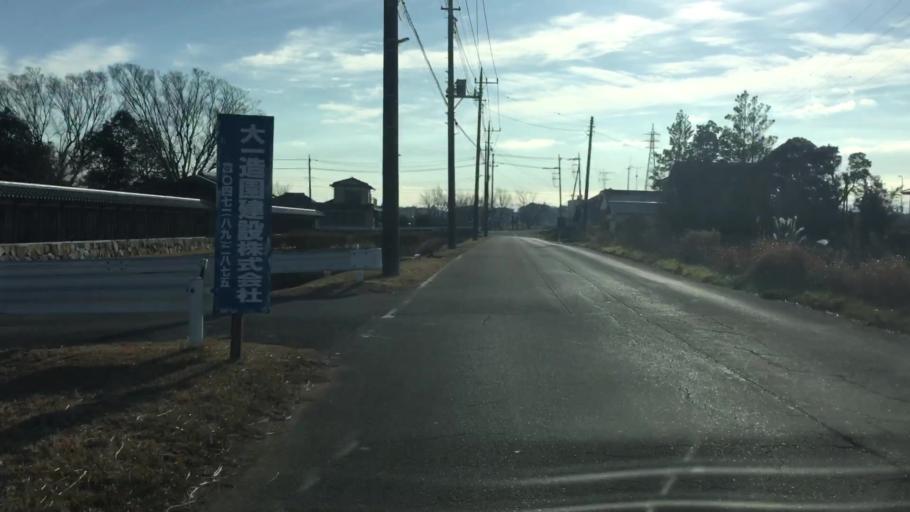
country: JP
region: Ibaraki
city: Toride
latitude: 35.8422
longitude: 140.1295
